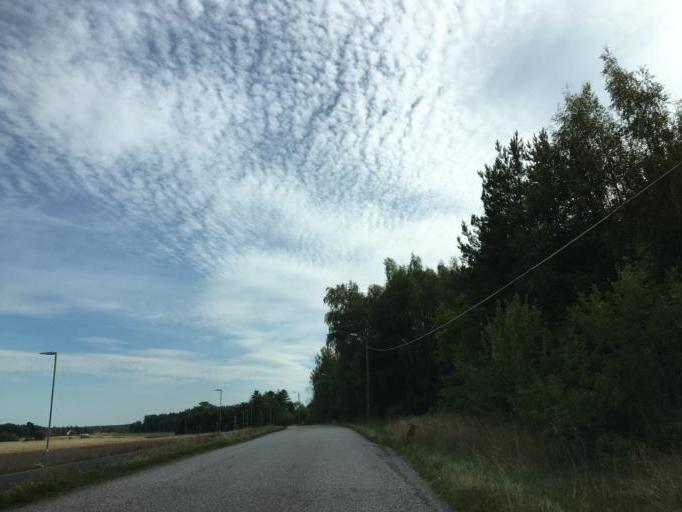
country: SE
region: Soedermanland
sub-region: Eskilstuna Kommun
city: Torshalla
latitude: 59.4472
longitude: 16.4688
